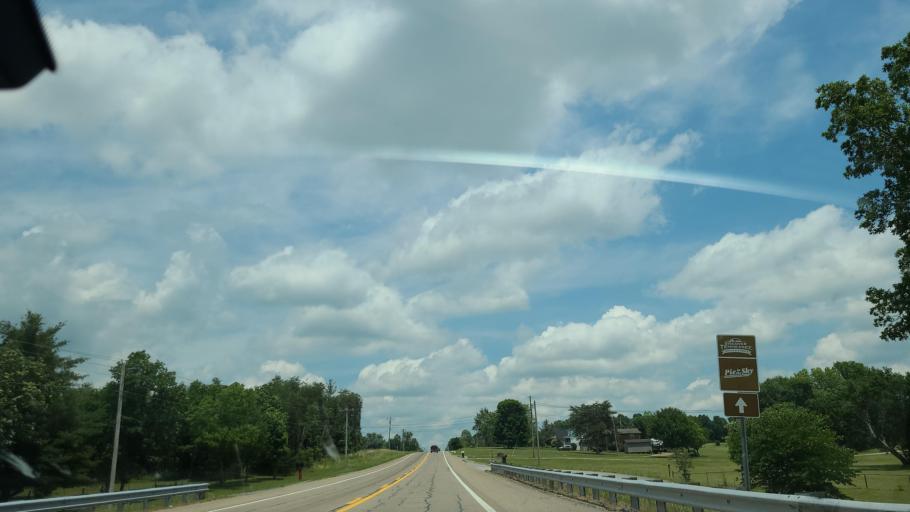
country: US
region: Tennessee
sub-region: Cumberland County
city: Lake Tansi
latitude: 35.8519
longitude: -85.0125
